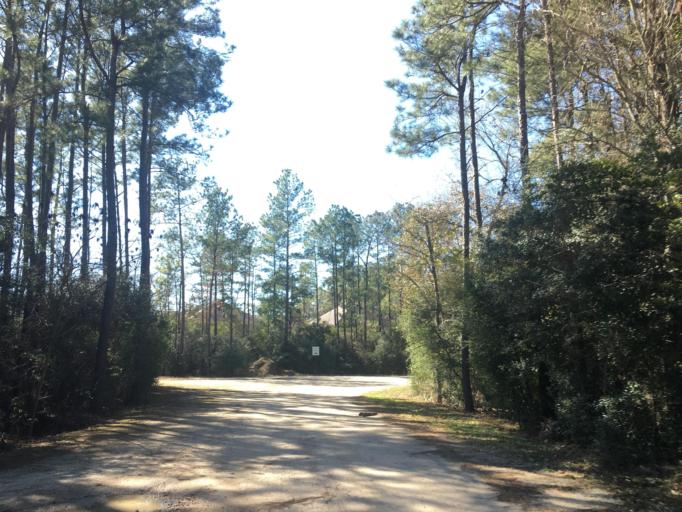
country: US
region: Texas
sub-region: Harris County
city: Spring
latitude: 30.0997
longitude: -95.4530
